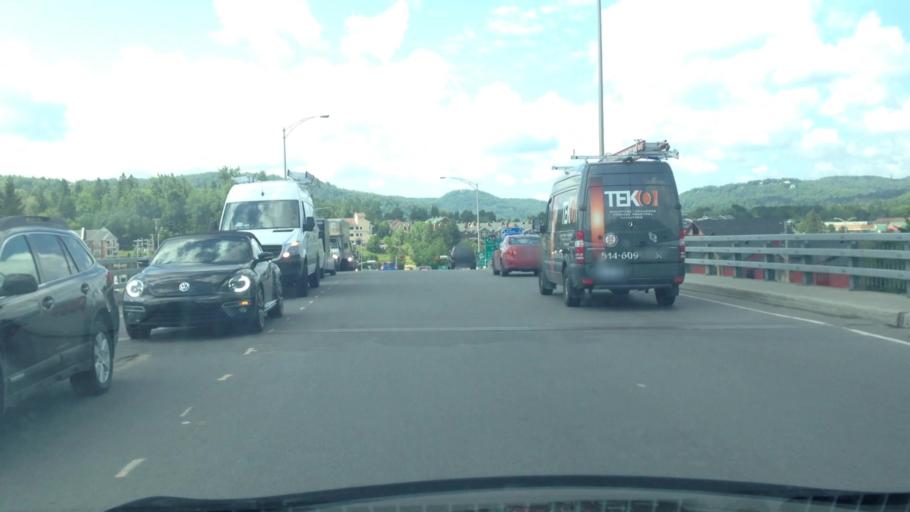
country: CA
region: Quebec
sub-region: Laurentides
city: Saint-Sauveur
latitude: 45.8917
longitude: -74.1460
